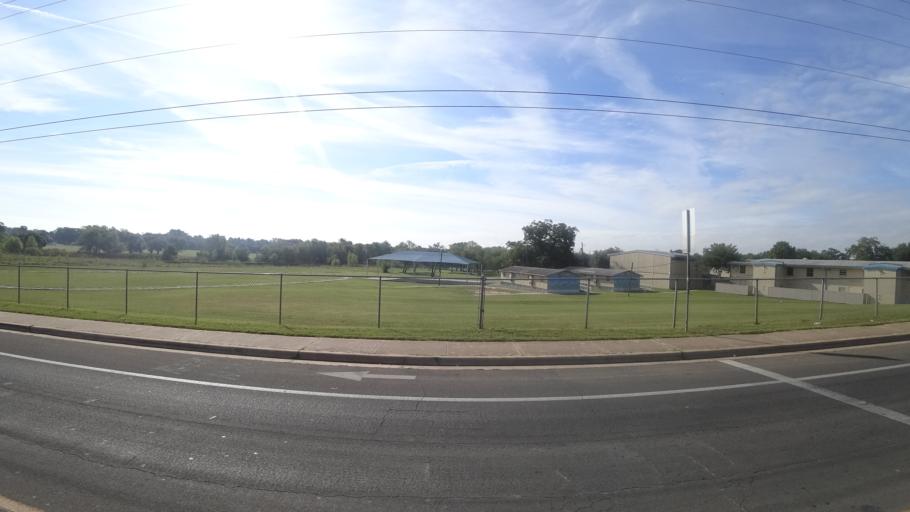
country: US
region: Texas
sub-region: Travis County
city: Austin
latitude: 30.2726
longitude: -97.7039
